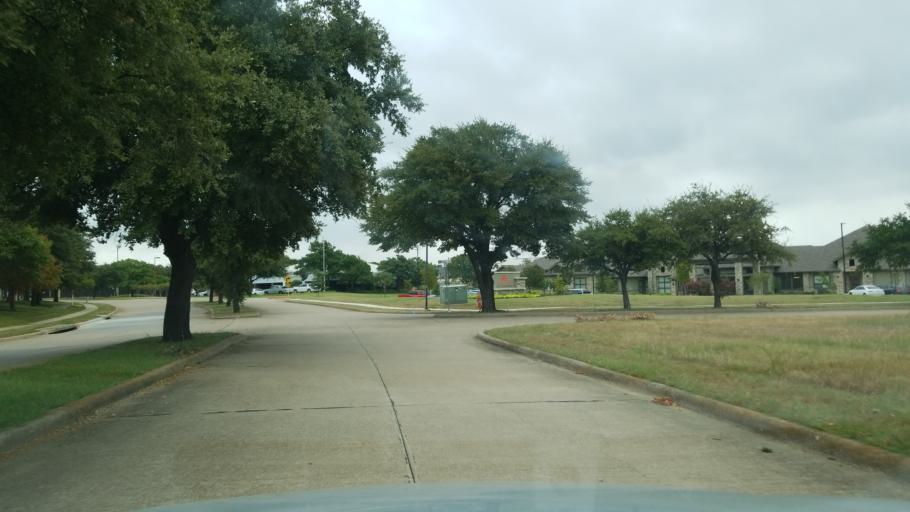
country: US
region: Texas
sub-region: Tarrant County
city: Bedford
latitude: 32.8415
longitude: -97.1138
